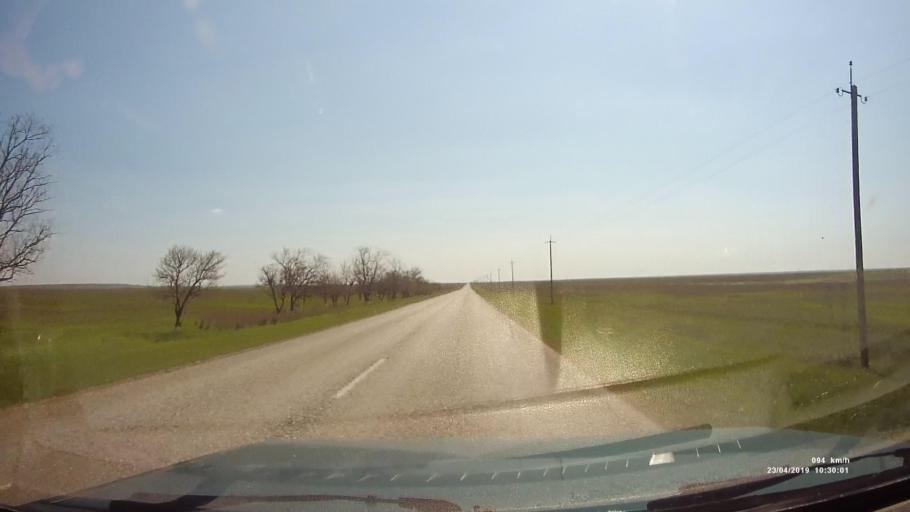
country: RU
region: Kalmykiya
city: Yashalta
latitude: 46.5950
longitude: 42.5366
